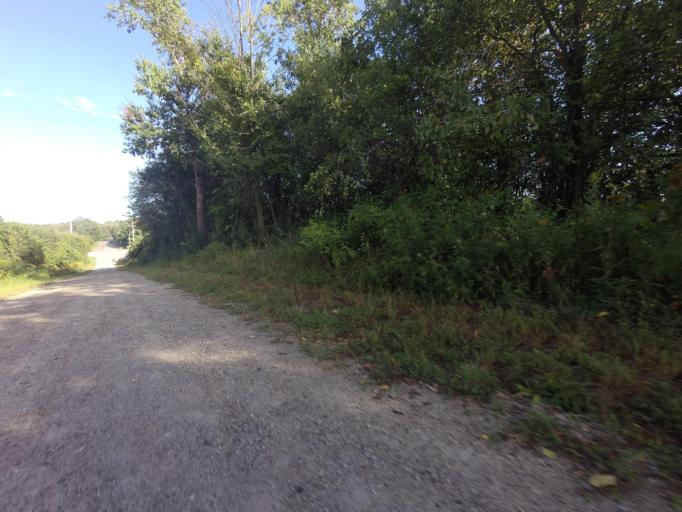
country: CA
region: Ontario
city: Waterloo
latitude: 43.6685
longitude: -80.4403
